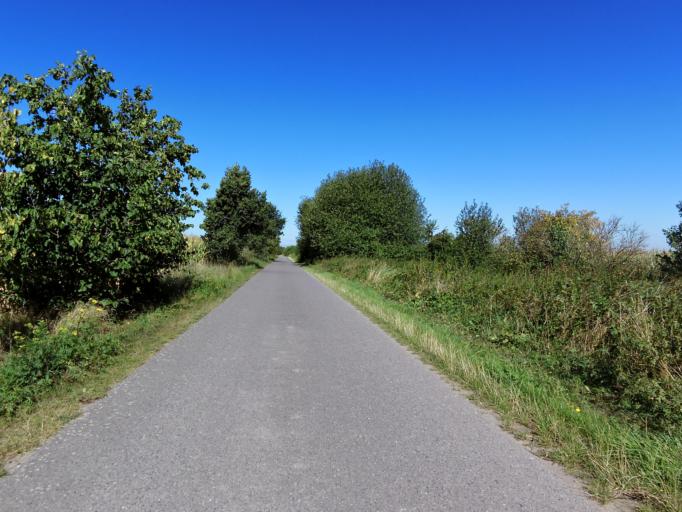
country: DE
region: Saxony
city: Dommitzsch
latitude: 51.6553
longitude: 12.8494
